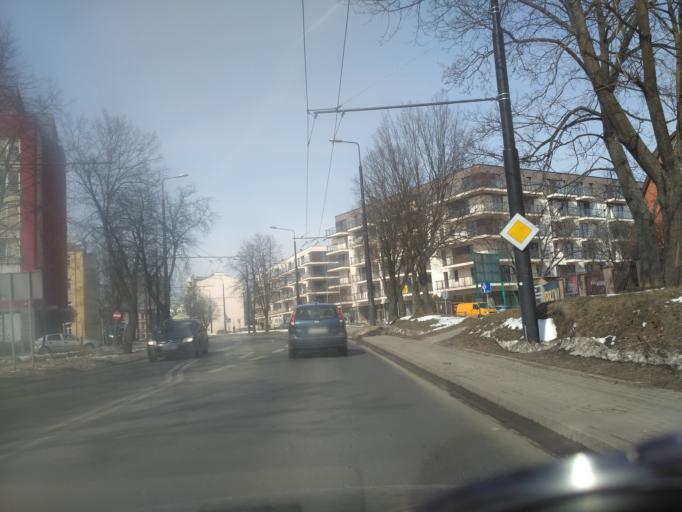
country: PL
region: Lublin Voivodeship
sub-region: Powiat lubelski
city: Lublin
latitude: 51.2572
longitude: 22.5743
